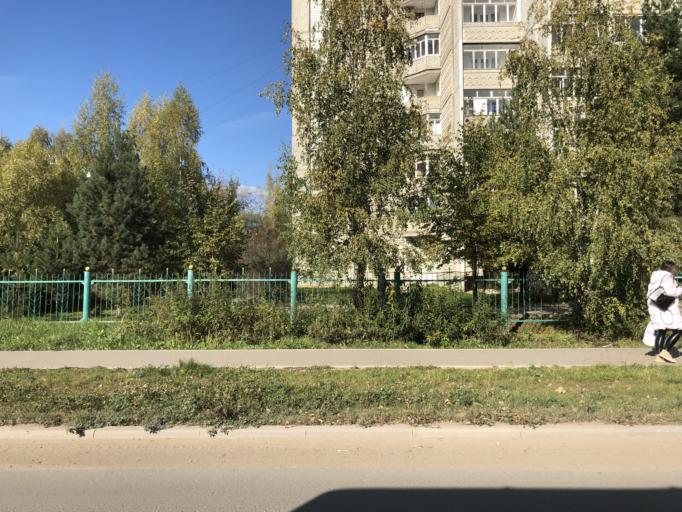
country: RU
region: Tverskaya
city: Rzhev
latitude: 56.2617
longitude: 34.3546
